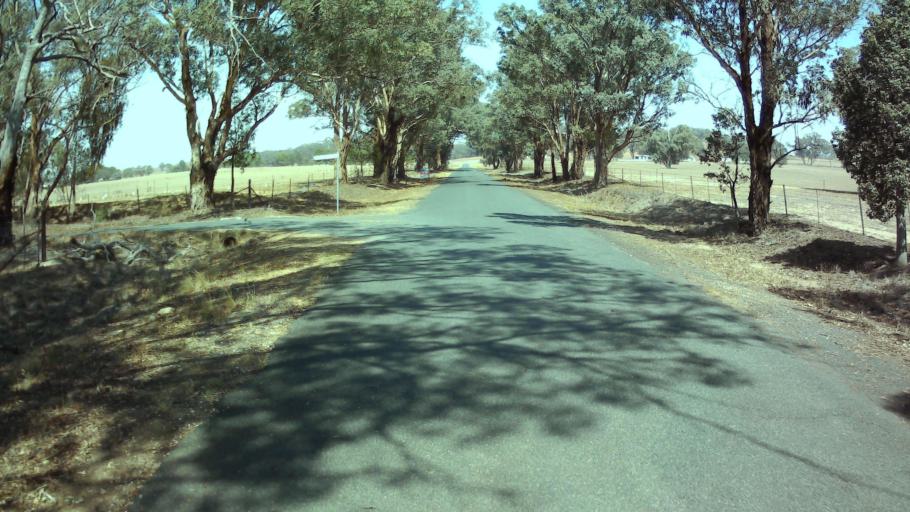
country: AU
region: New South Wales
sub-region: Weddin
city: Grenfell
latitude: -33.8956
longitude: 148.1437
